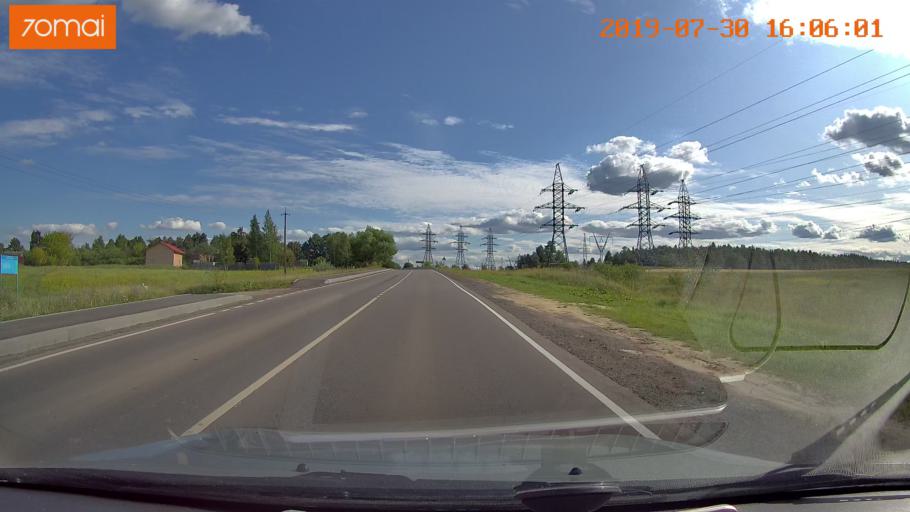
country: RU
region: Moskovskaya
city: Peski
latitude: 55.2598
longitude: 38.7155
